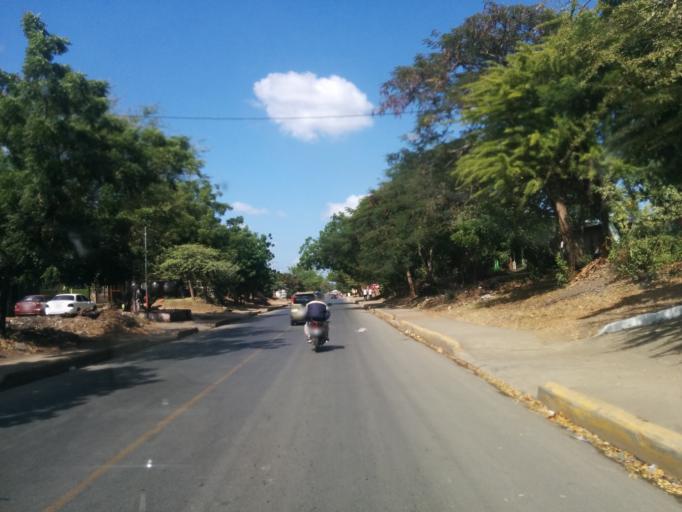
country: NI
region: Managua
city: Tipitapa
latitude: 12.1817
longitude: -86.0961
